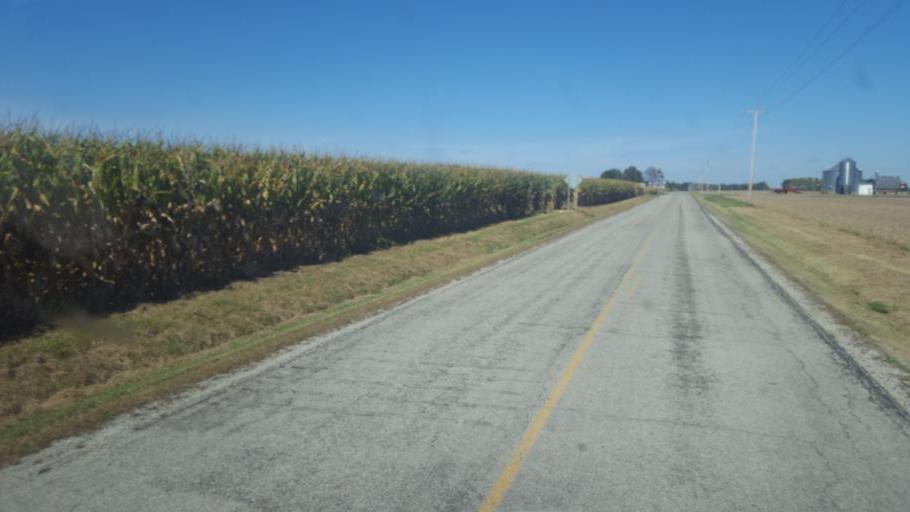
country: US
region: Ohio
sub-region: Huron County
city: Willard
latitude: 40.9730
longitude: -82.7907
